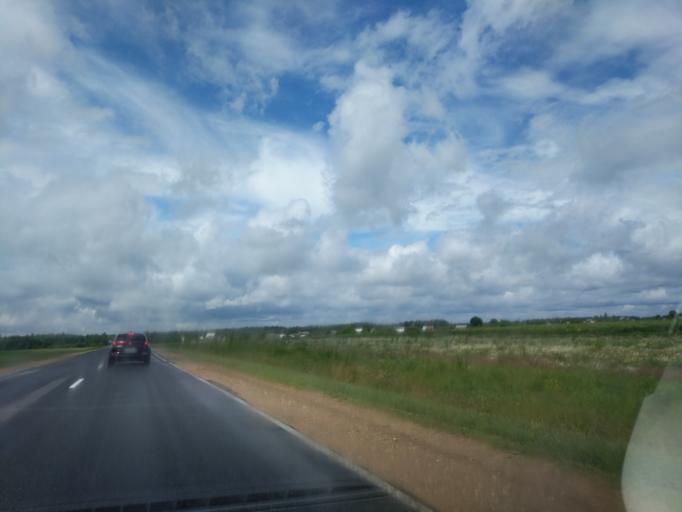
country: BY
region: Minsk
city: Il'ya
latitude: 54.3936
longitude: 27.3435
